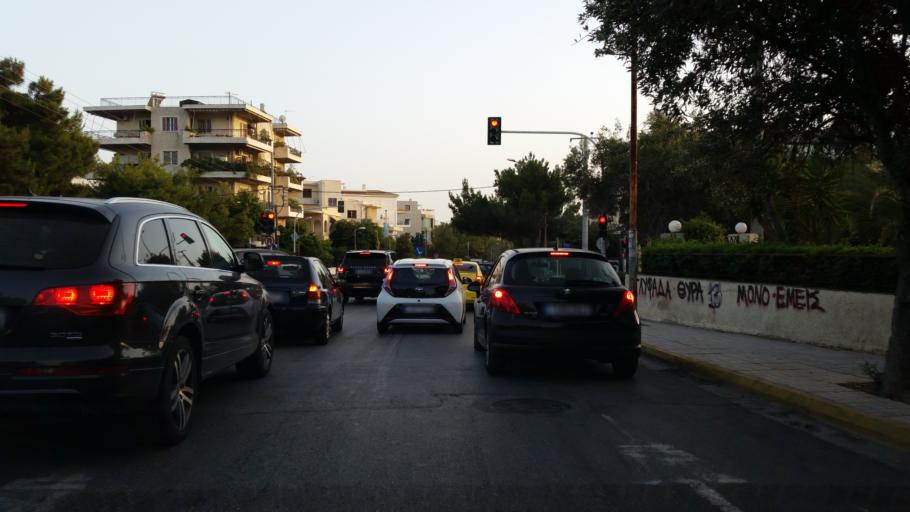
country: GR
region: Attica
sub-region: Nomarchia Athinas
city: Glyfada
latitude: 37.8671
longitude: 23.7571
